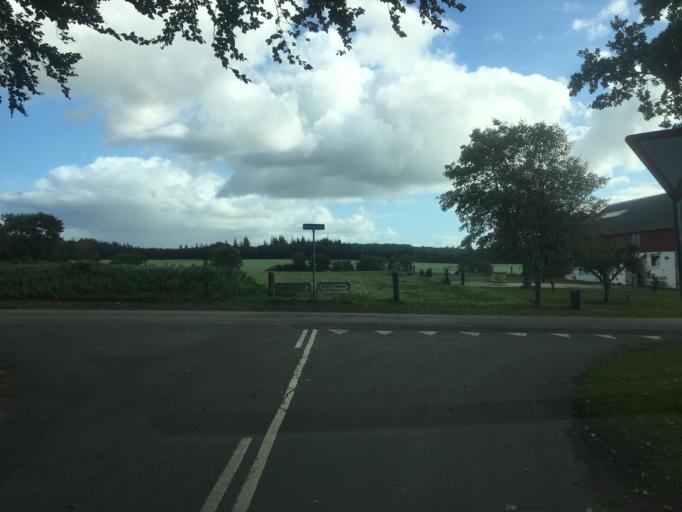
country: DK
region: South Denmark
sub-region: Tonder Kommune
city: Logumkloster
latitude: 55.1138
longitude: 8.8832
